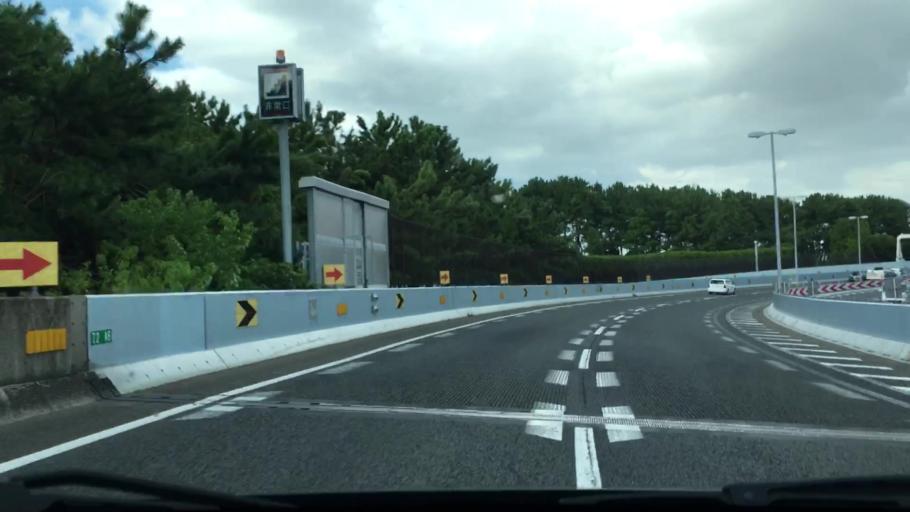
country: JP
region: Fukuoka
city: Fukuoka-shi
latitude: 33.5926
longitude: 130.3460
